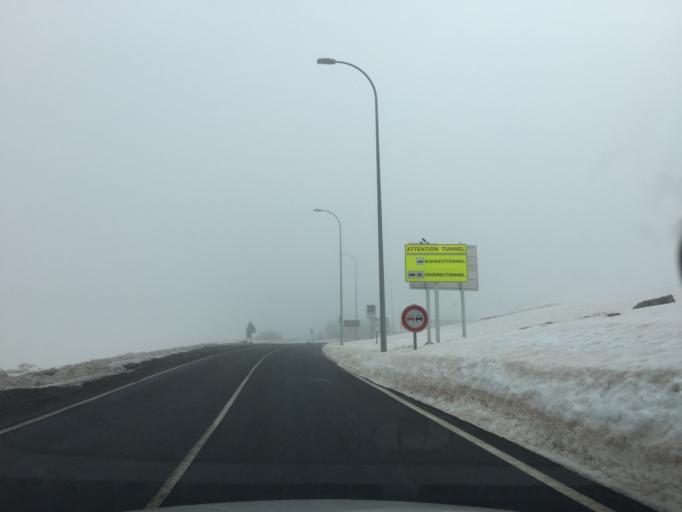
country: ES
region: Aragon
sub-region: Provincia de Huesca
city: Bielsa
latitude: 42.7496
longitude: 0.1904
